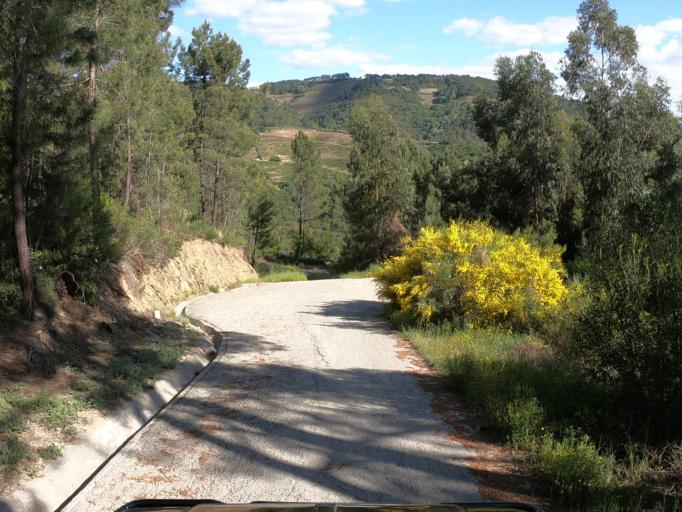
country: PT
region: Vila Real
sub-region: Vila Real
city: Vila Real
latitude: 41.2766
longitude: -7.7480
